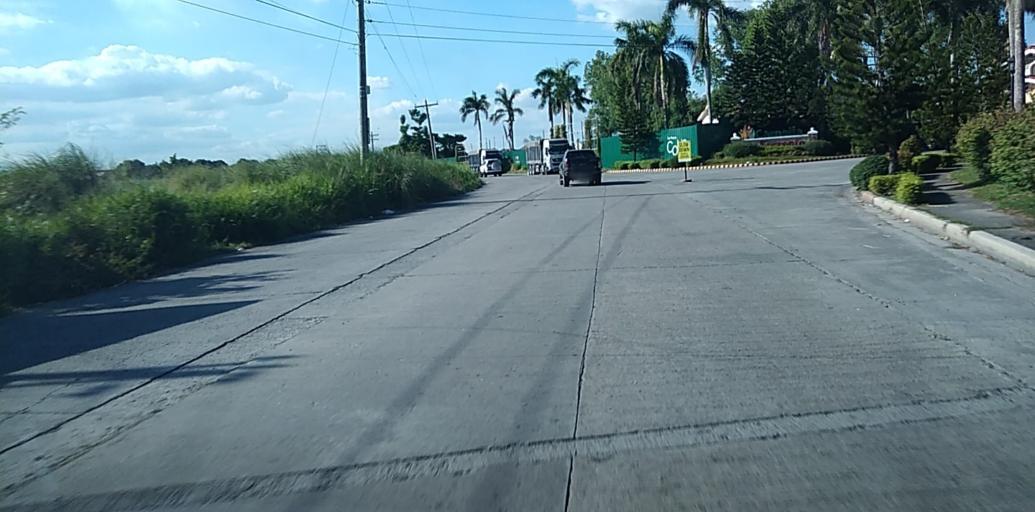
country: PH
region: Central Luzon
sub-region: Province of Pampanga
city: Acli
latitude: 15.1092
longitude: 120.6533
